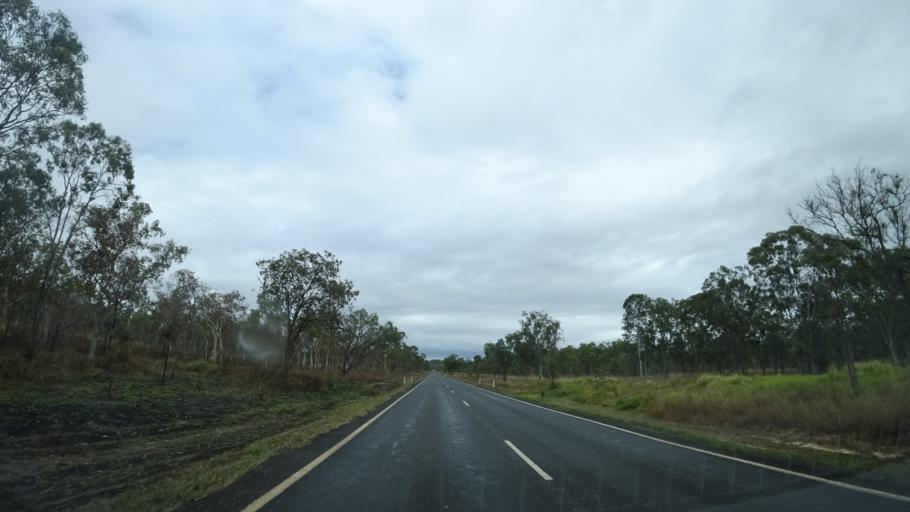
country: AU
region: Queensland
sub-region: Tablelands
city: Mareeba
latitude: -16.7650
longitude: 145.3413
